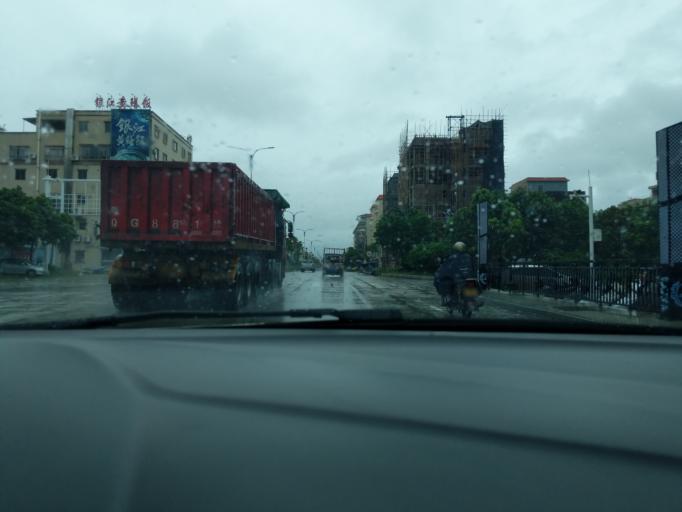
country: CN
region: Guangdong
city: Pingshi
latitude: 22.2040
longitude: 112.3264
